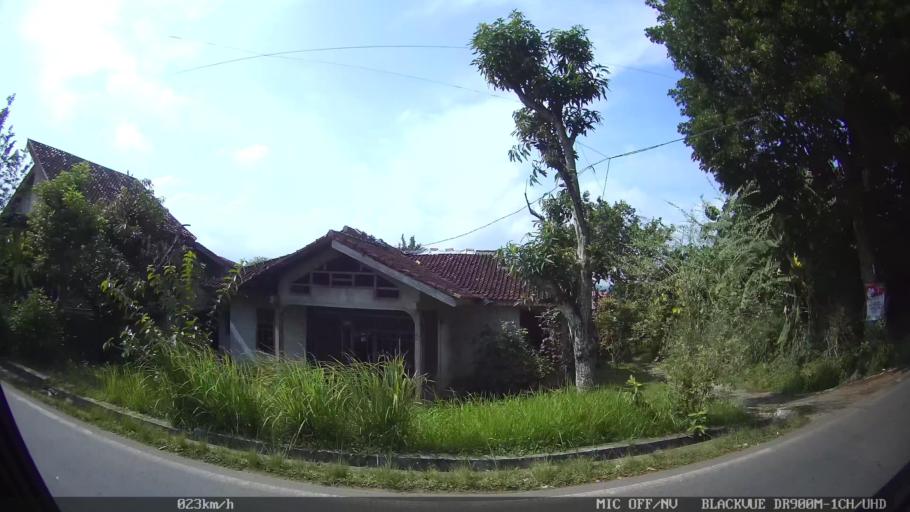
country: ID
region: Lampung
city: Kedaton
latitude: -5.3657
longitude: 105.2306
